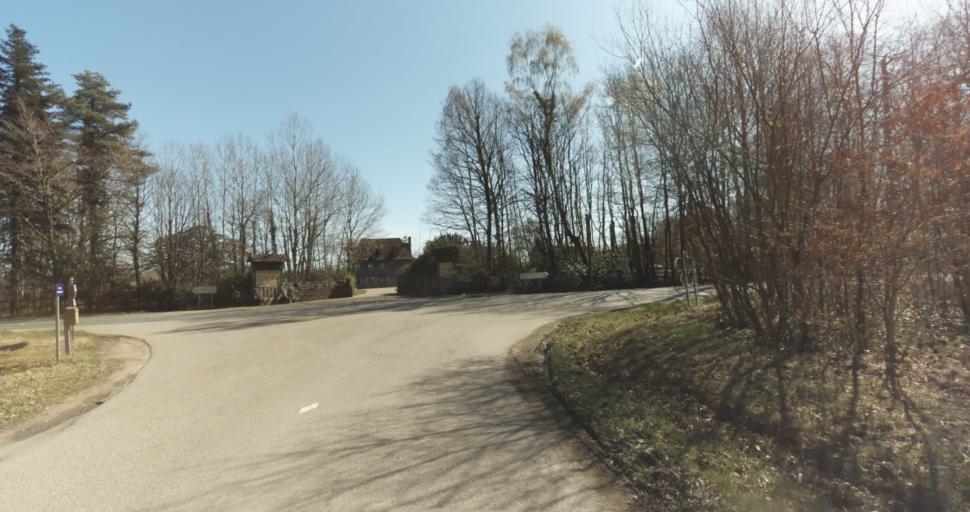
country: FR
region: Lower Normandy
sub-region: Departement du Calvados
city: Livarot
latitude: 48.9658
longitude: 0.0976
